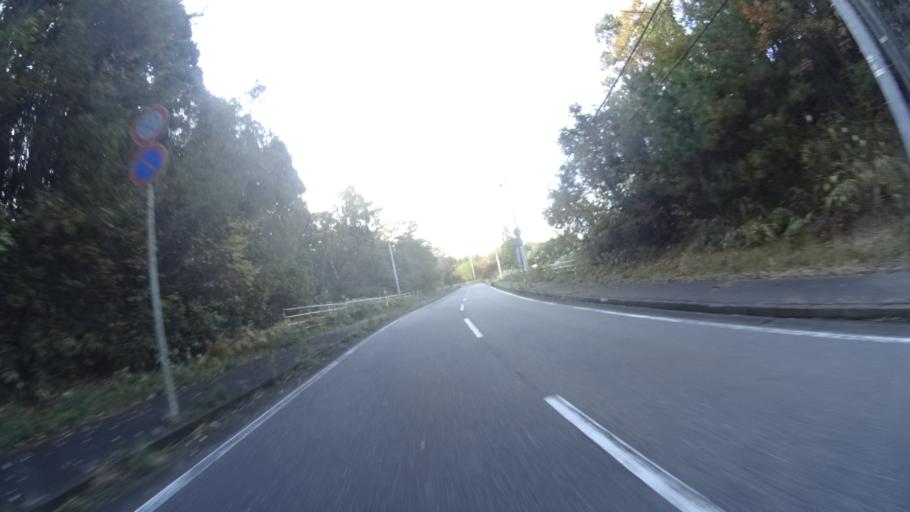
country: JP
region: Ishikawa
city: Hakui
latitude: 37.0658
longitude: 136.7667
